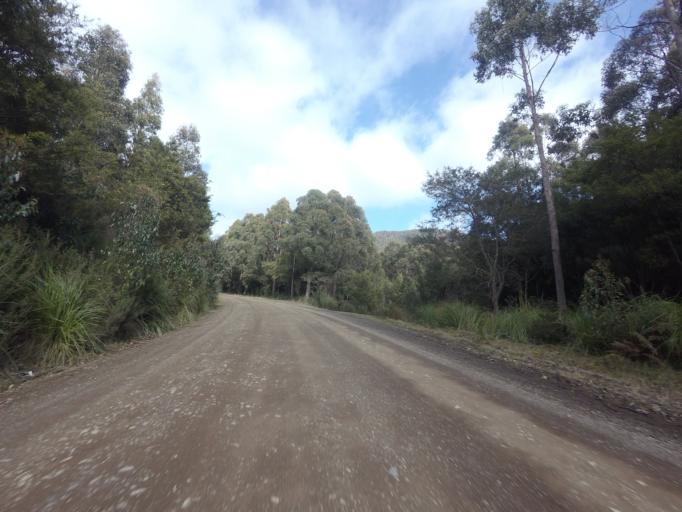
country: AU
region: Tasmania
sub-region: Huon Valley
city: Geeveston
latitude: -43.4680
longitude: 146.8944
